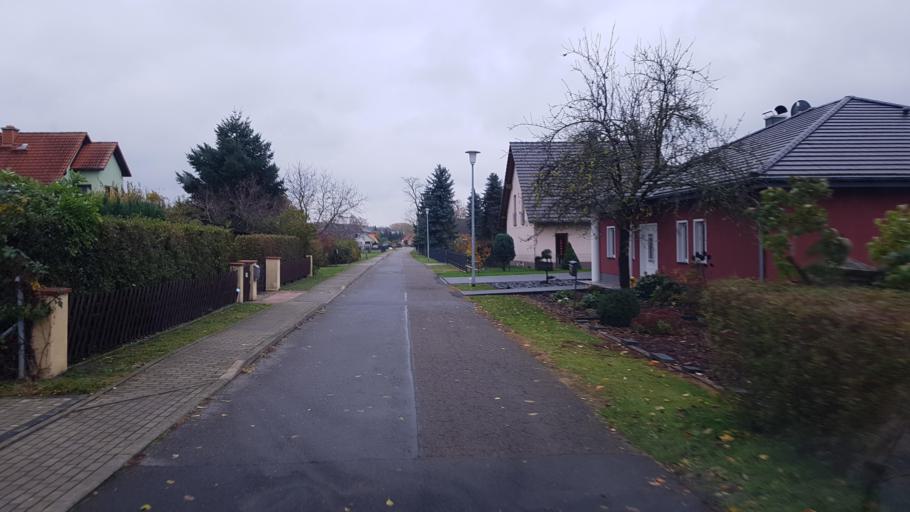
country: DE
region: Brandenburg
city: Drebkau
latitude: 51.6968
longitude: 14.2494
